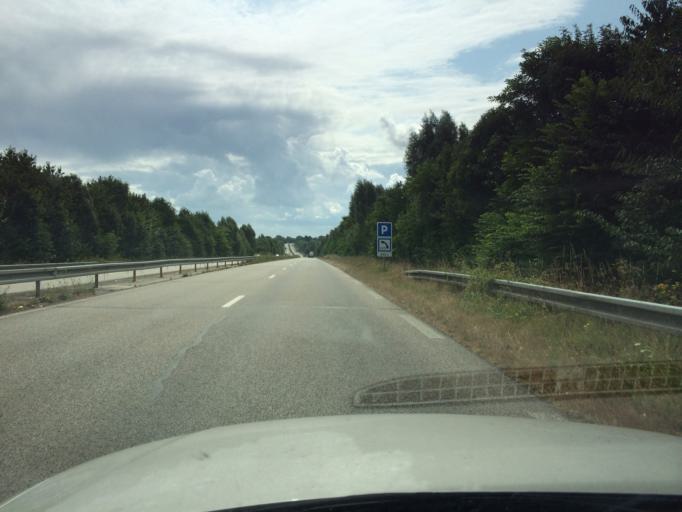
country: FR
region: Lower Normandy
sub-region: Departement de la Manche
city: Montebourg
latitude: 49.4814
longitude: -1.3876
